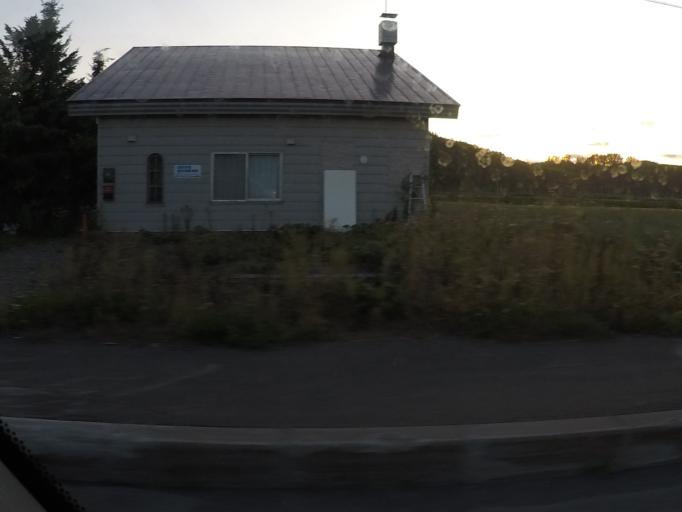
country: JP
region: Hokkaido
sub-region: Asahikawa-shi
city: Asahikawa
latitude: 43.6470
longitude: 142.4481
